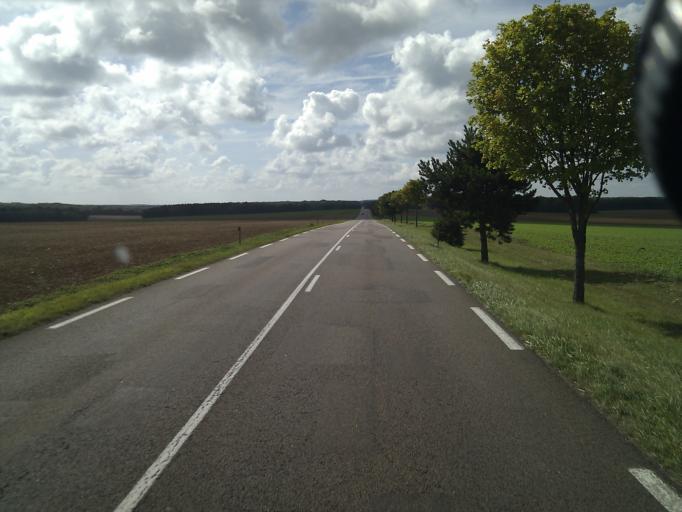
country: FR
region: Bourgogne
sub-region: Departement de la Cote-d'Or
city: Montbard
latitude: 47.6993
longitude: 4.4255
